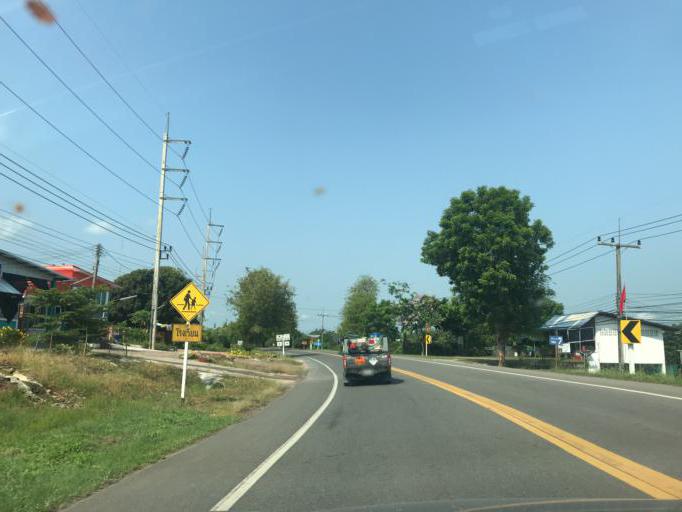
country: TH
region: Phayao
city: Chiang Kham
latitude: 19.4695
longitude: 100.2120
